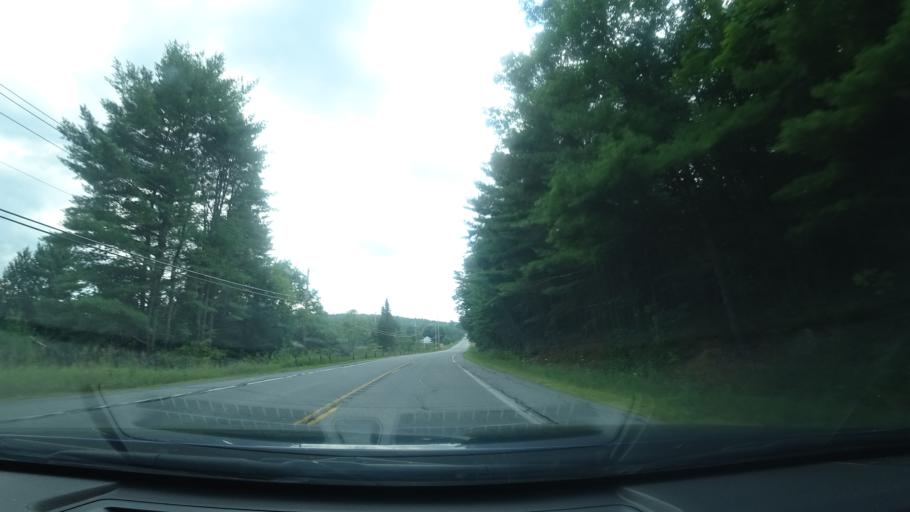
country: US
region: New York
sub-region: Warren County
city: Warrensburg
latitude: 43.5231
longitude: -73.7888
